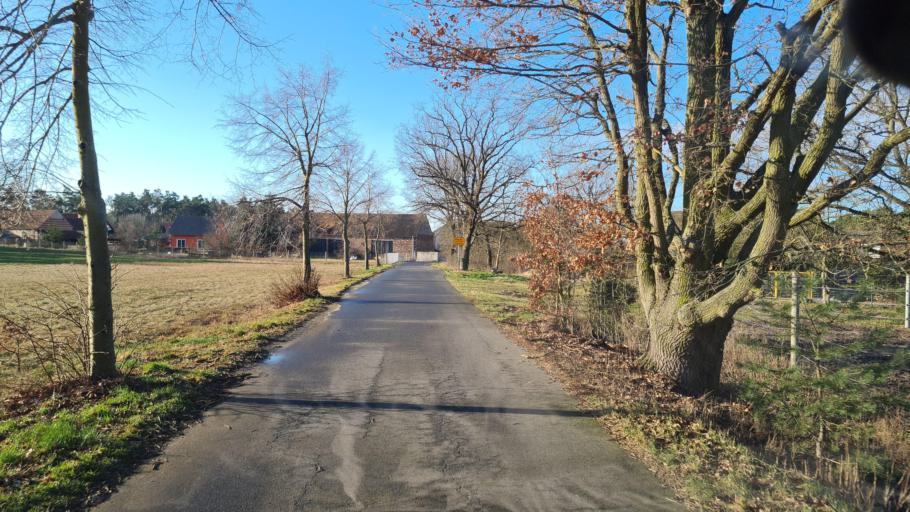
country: DE
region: Brandenburg
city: Herzberg
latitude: 51.6982
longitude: 13.1770
